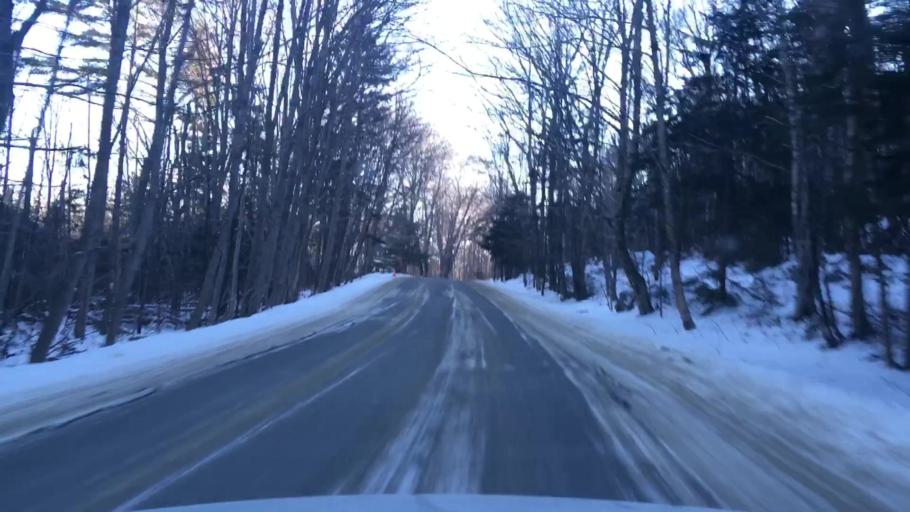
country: US
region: Maine
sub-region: Hancock County
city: Castine
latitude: 44.3483
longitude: -68.7827
